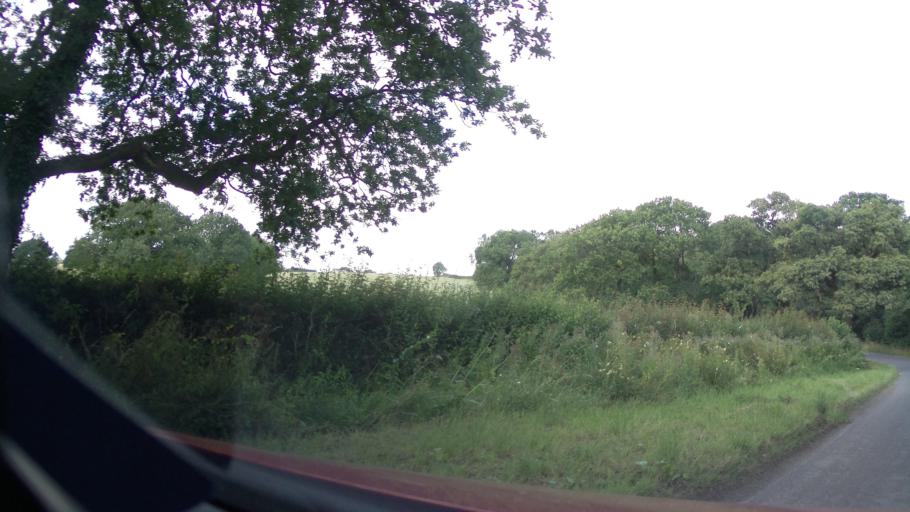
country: GB
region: England
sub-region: Wiltshire
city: Hankerton
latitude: 51.5794
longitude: -2.0096
